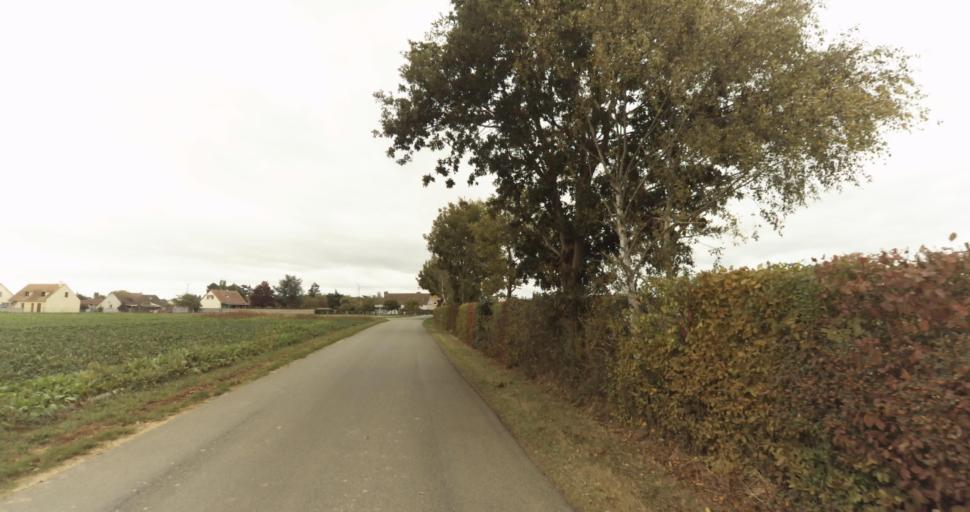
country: FR
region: Centre
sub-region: Departement d'Eure-et-Loir
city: Treon
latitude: 48.6751
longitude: 1.3684
